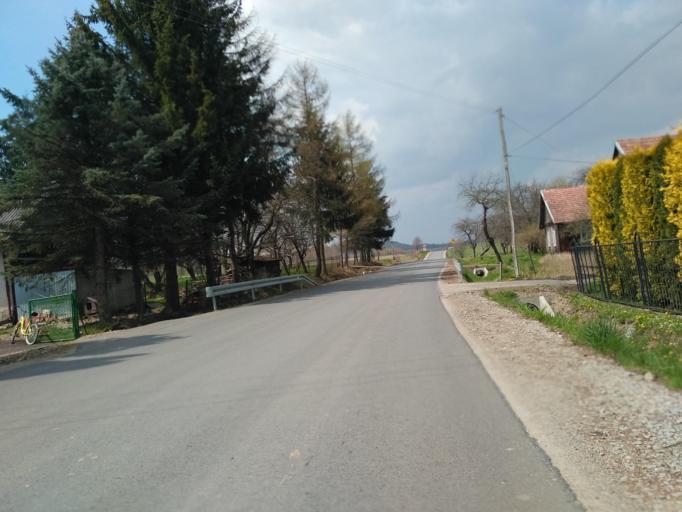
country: PL
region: Subcarpathian Voivodeship
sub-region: Powiat sanocki
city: Strachocina
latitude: 49.5877
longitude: 22.1117
